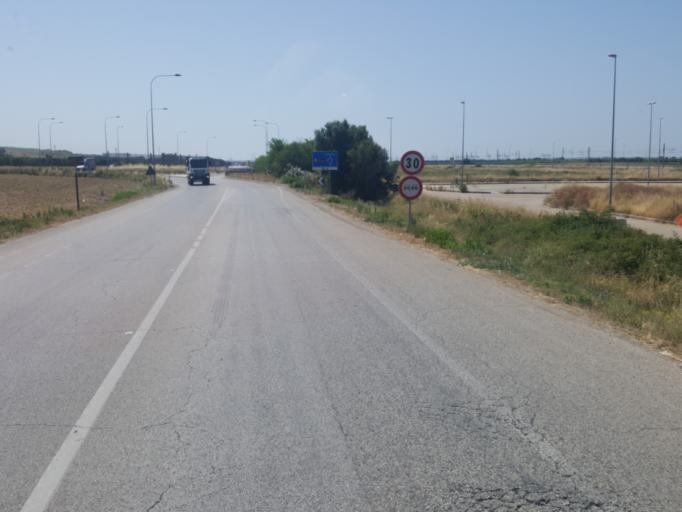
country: IT
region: Apulia
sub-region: Provincia di Taranto
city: Massafra
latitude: 40.5578
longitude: 17.1361
